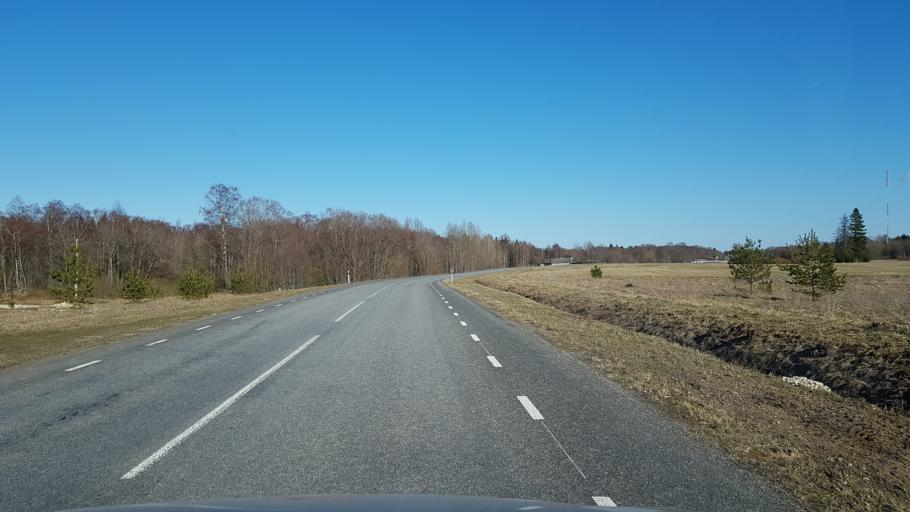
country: EE
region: Laeaene-Virumaa
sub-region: Haljala vald
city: Haljala
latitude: 59.4587
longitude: 26.2181
